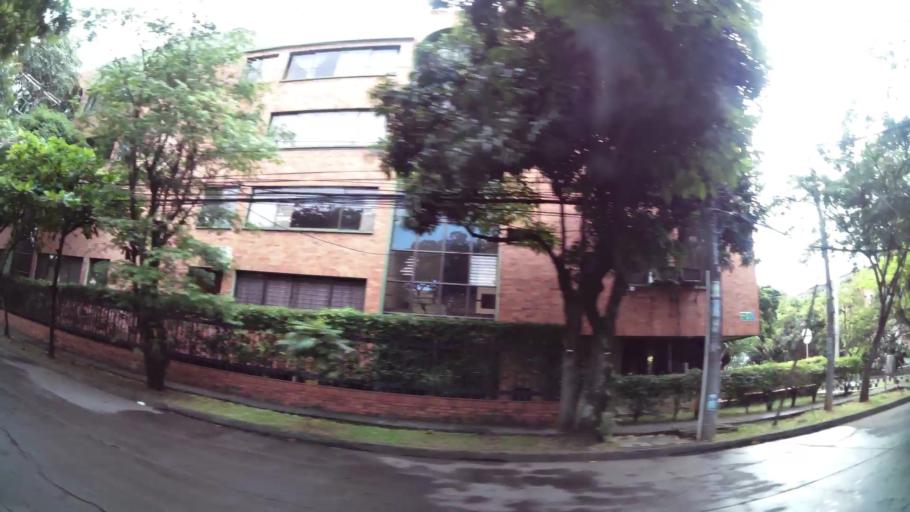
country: CO
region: Valle del Cauca
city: Cali
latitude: 3.4718
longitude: -76.5229
